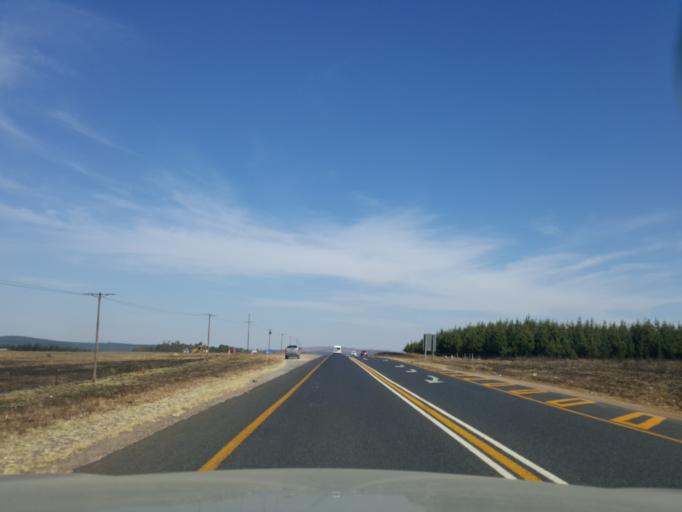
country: ZA
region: Mpumalanga
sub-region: Nkangala District Municipality
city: Belfast
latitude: -25.5341
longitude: 30.3367
